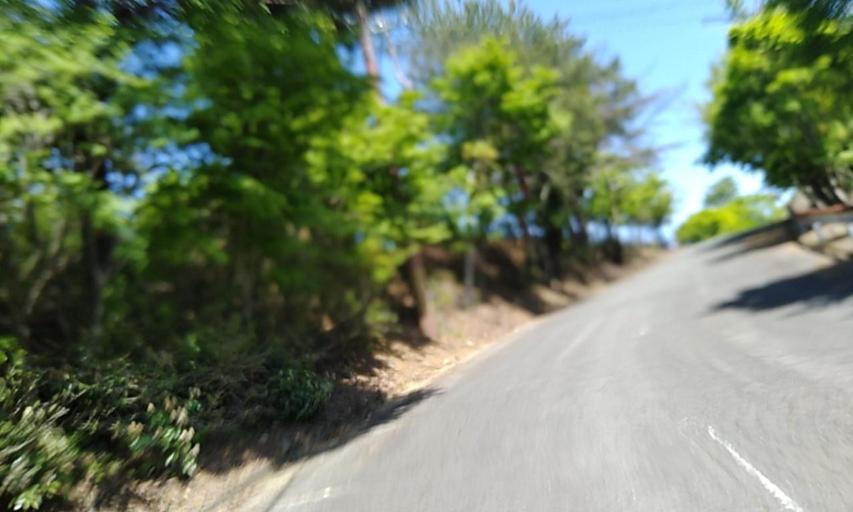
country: JP
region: Fukui
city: Obama
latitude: 35.5600
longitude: 135.7296
